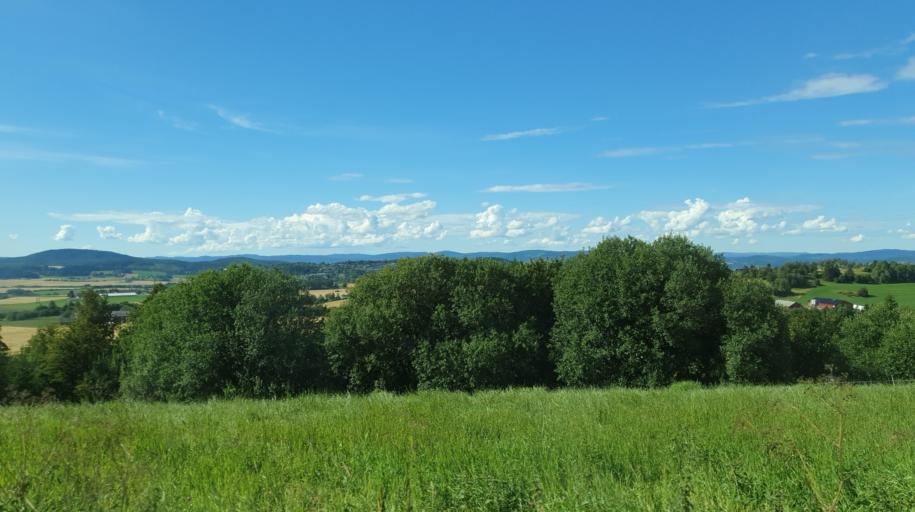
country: NO
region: Nord-Trondelag
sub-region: Levanger
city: Skogn
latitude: 63.6933
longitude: 11.2331
